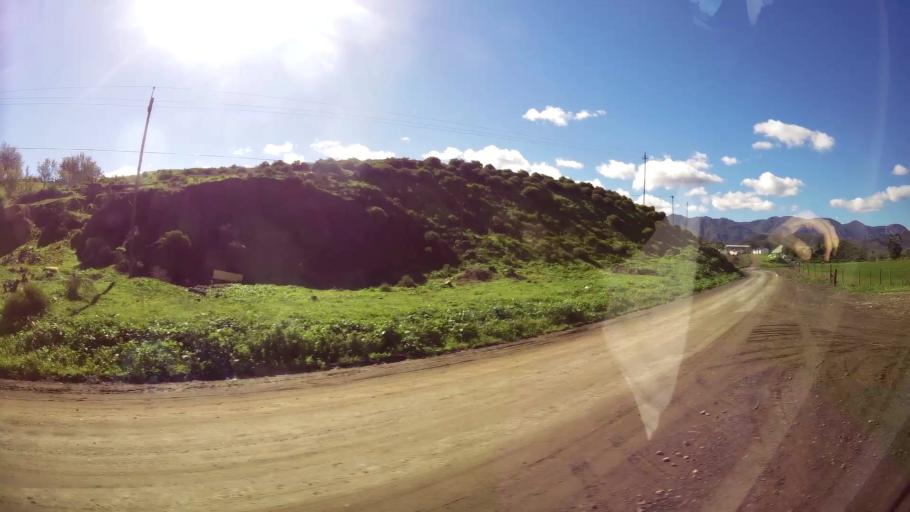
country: ZA
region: Western Cape
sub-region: Cape Winelands District Municipality
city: Ashton
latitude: -33.7937
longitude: 19.9005
